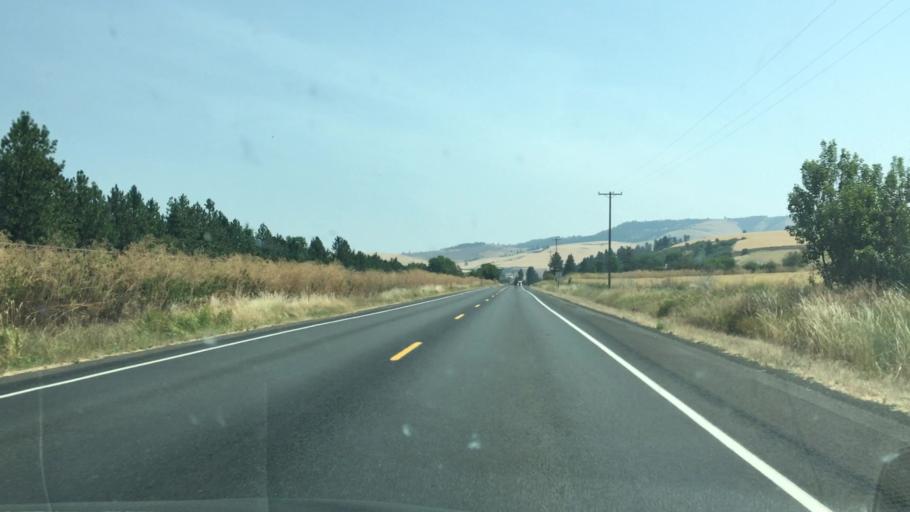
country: US
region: Idaho
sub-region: Nez Perce County
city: Lapwai
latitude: 46.3728
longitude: -116.6943
